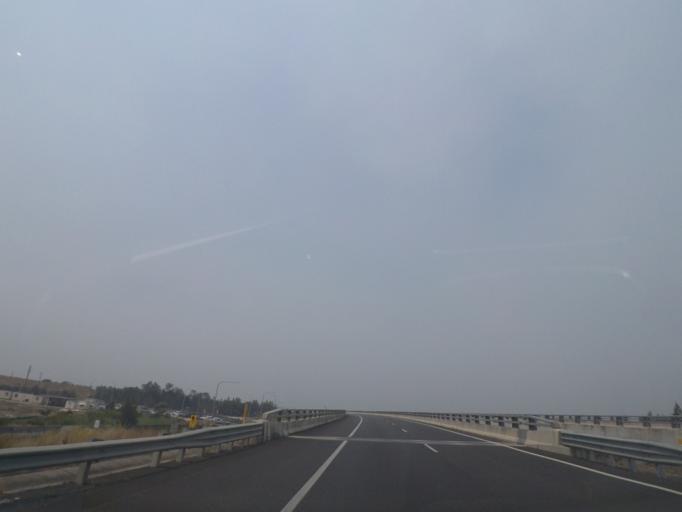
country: AU
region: New South Wales
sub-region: Ballina
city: Ballina
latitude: -28.8619
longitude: 153.5179
